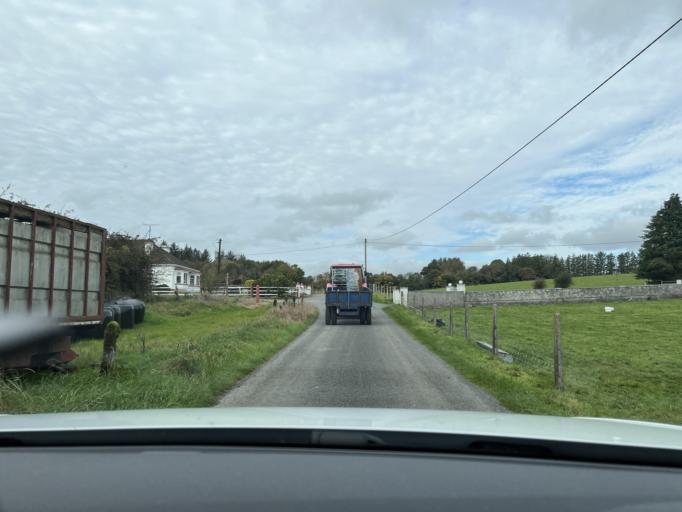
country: IE
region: Connaught
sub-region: Roscommon
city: Boyle
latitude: 53.9798
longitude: -8.2260
